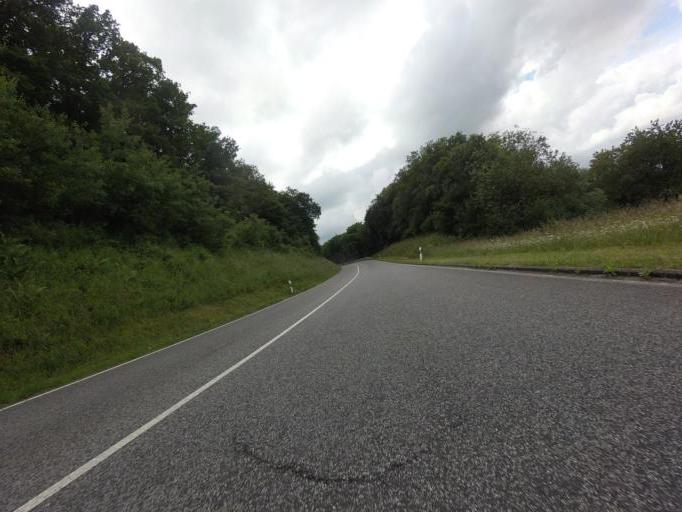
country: DE
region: Rheinland-Pfalz
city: Monreal
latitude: 50.2917
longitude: 7.1506
